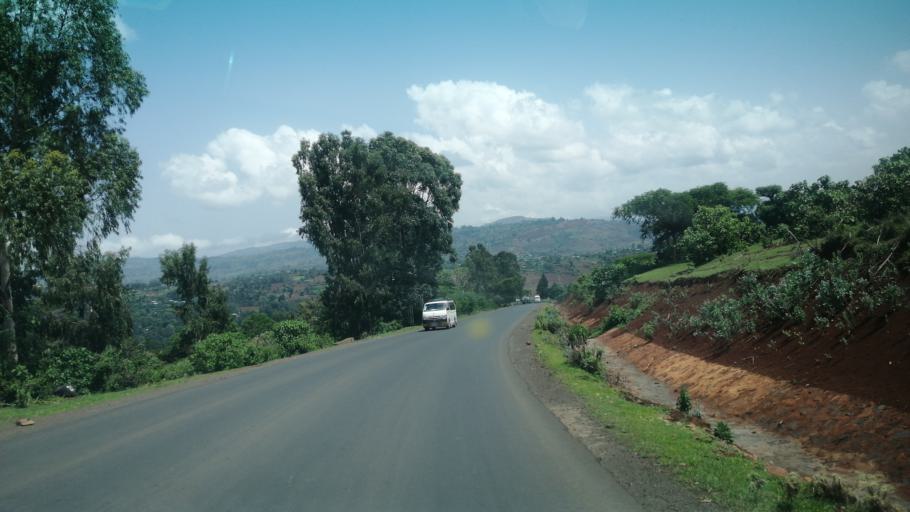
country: ET
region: Oromiya
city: Gedo
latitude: 8.9751
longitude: 37.5640
